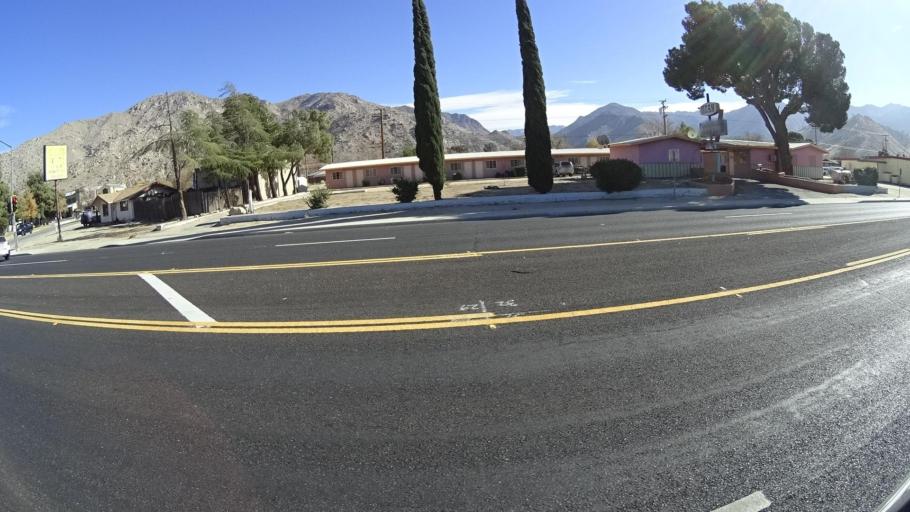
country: US
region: California
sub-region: Kern County
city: Lake Isabella
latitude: 35.6161
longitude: -118.4787
